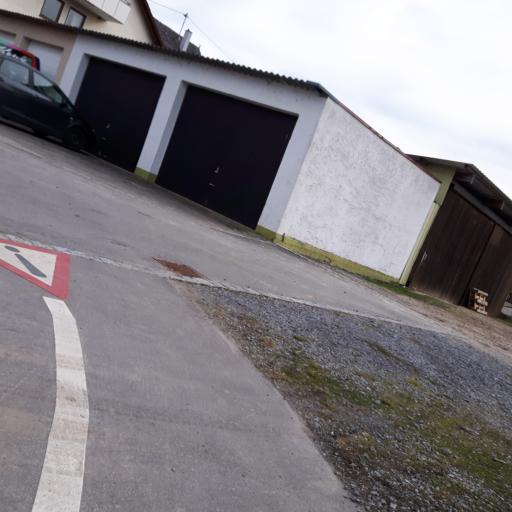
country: DE
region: Baden-Wuerttemberg
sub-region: Regierungsbezirk Stuttgart
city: Ilsfeld
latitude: 49.0526
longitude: 9.2443
